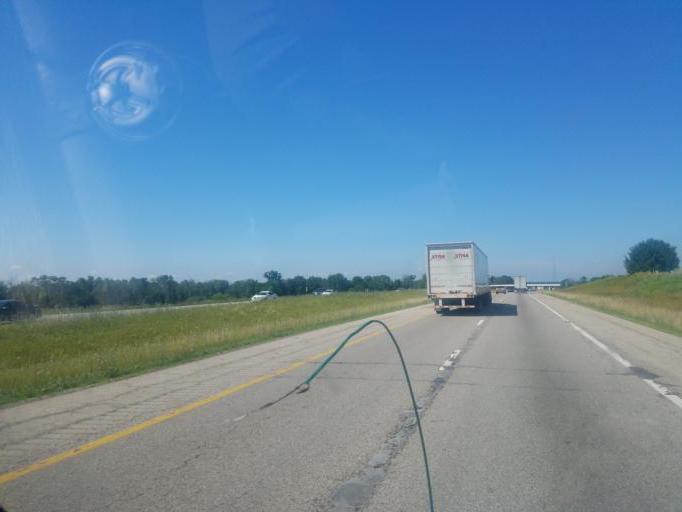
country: US
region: Ohio
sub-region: Warren County
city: Waynesville
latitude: 39.4614
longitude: -83.9879
